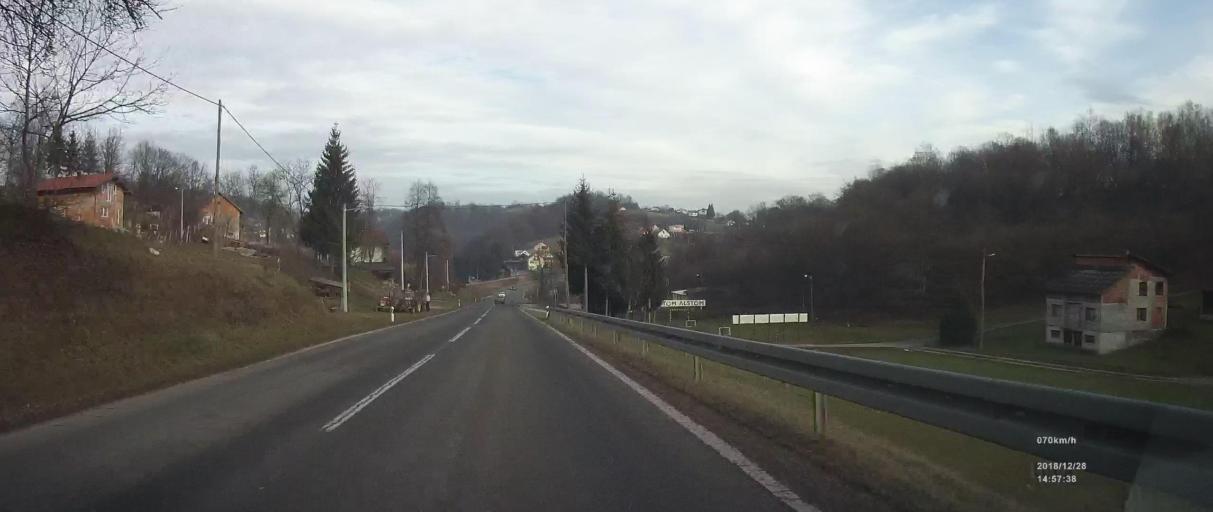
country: HR
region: Karlovacka
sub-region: Grad Karlovac
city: Karlovac
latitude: 45.4550
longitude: 15.4592
